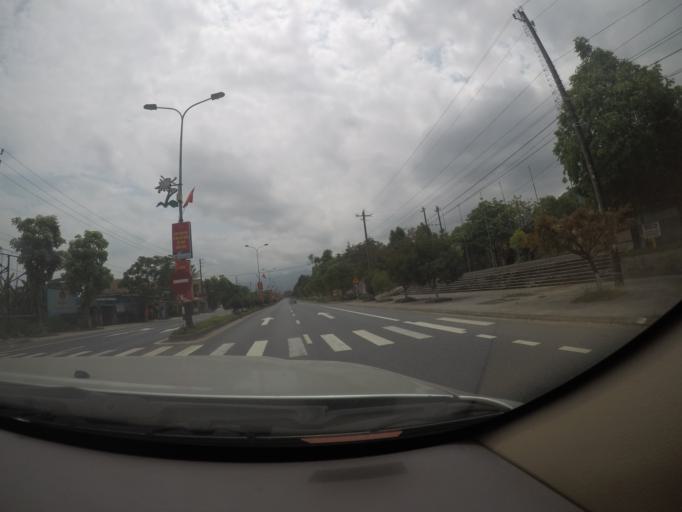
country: VN
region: Thua Thien-Hue
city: Phu Loc
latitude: 16.2826
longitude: 107.8586
